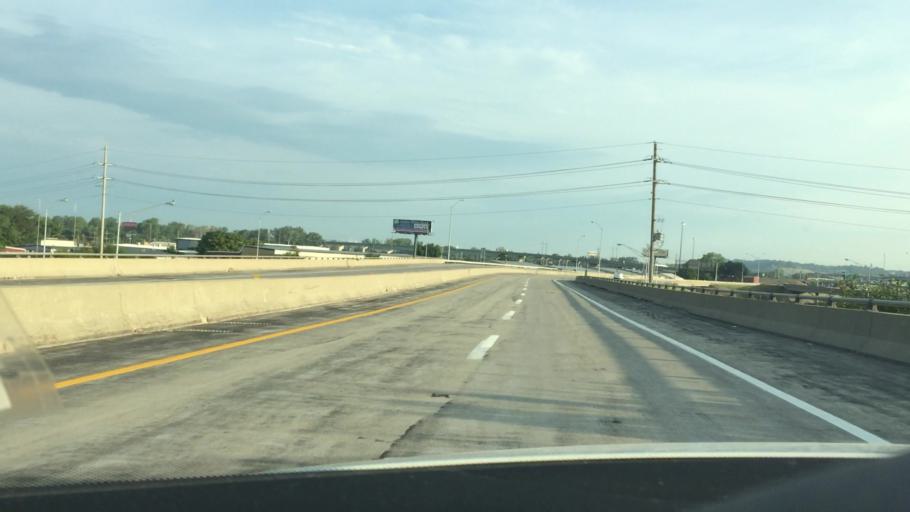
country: US
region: Kansas
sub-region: Doniphan County
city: Elwood
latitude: 39.7404
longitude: -94.8521
